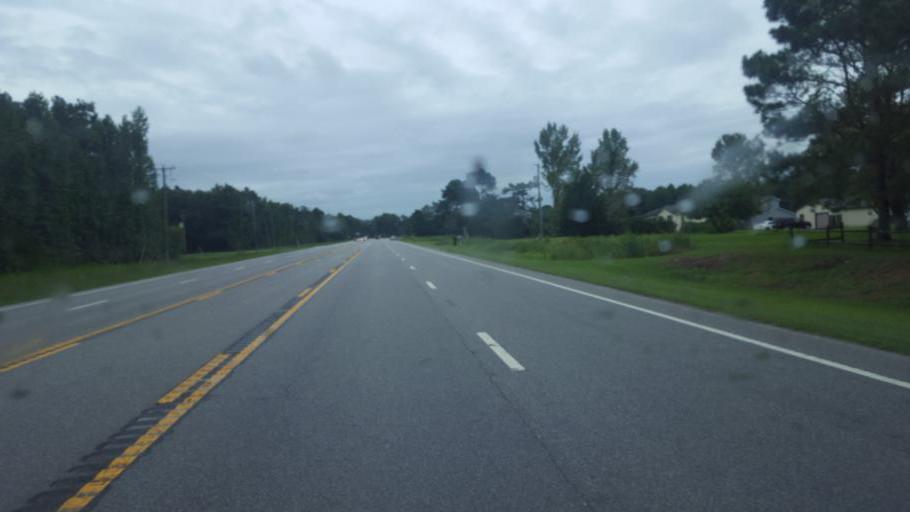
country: US
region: North Carolina
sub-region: Currituck County
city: Currituck
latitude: 36.4212
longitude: -76.0049
